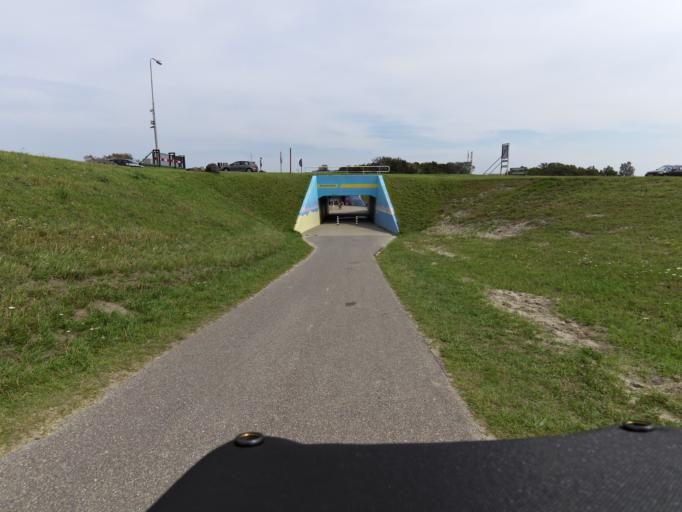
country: NL
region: Zeeland
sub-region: Schouwen-Duiveland
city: Scharendijke
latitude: 51.7391
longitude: 3.8234
